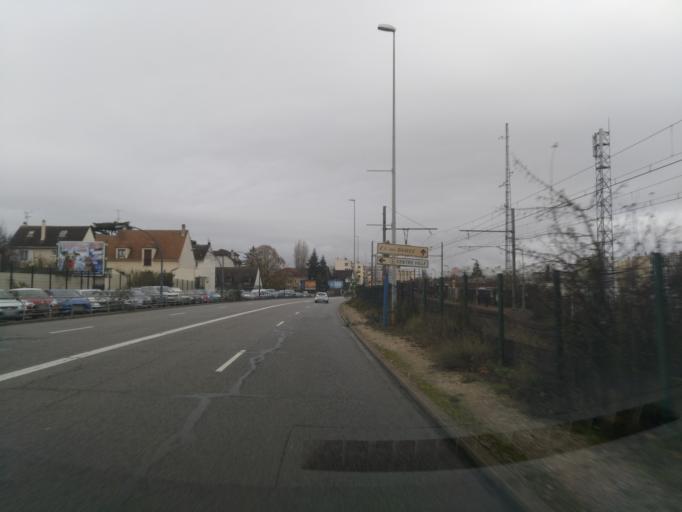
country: FR
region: Ile-de-France
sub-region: Departement des Yvelines
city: Villepreux
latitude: 48.8227
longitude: 1.9942
